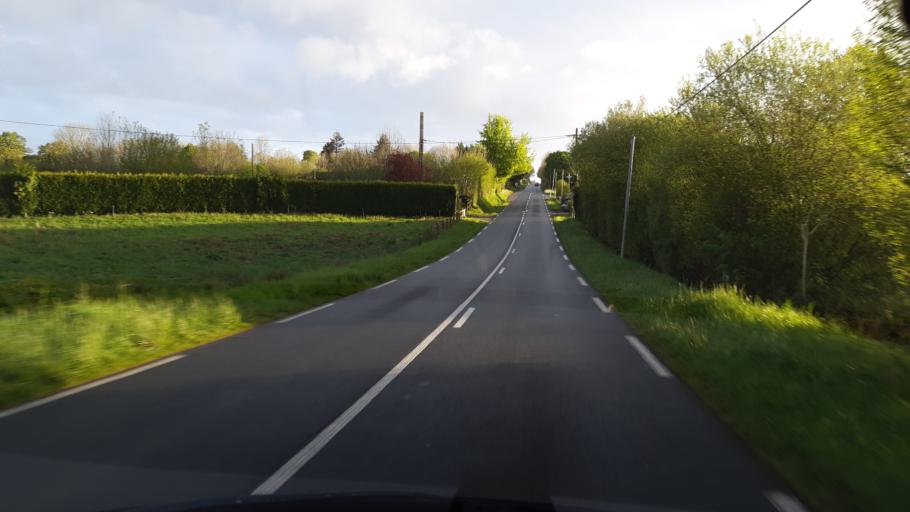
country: FR
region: Lower Normandy
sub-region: Departement de la Manche
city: Tessy-sur-Vire
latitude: 49.0210
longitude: -1.1468
